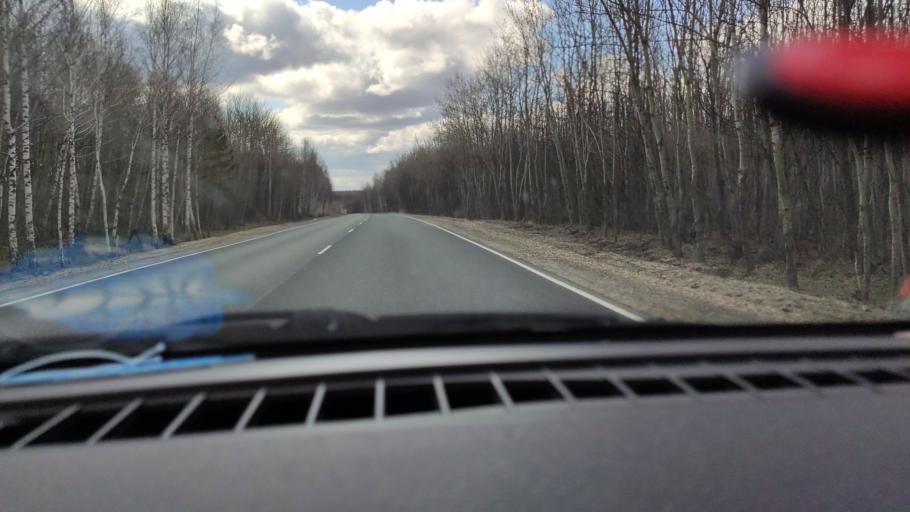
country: RU
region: Saratov
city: Khvalynsk
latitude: 52.4431
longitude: 48.0097
